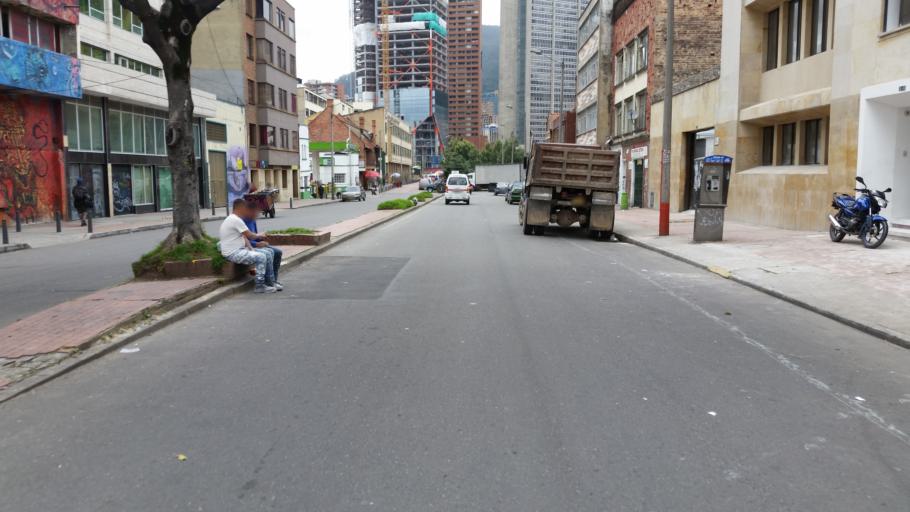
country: CO
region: Bogota D.C.
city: Bogota
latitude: 4.6141
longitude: -74.0750
